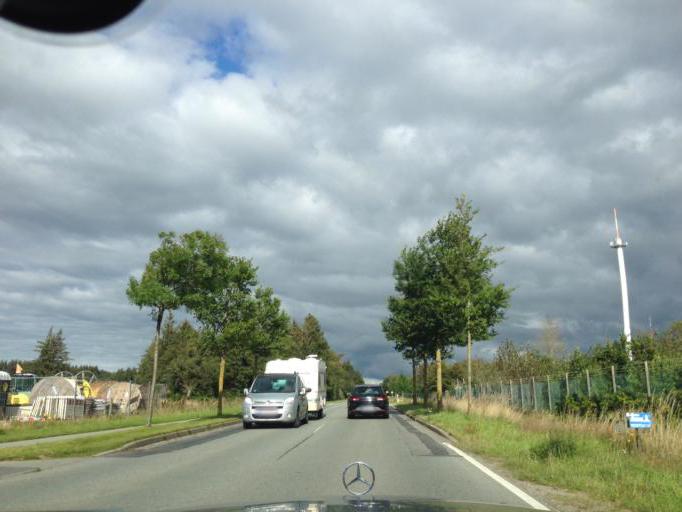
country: DE
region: Schleswig-Holstein
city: Stedesand
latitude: 54.7392
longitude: 8.9533
